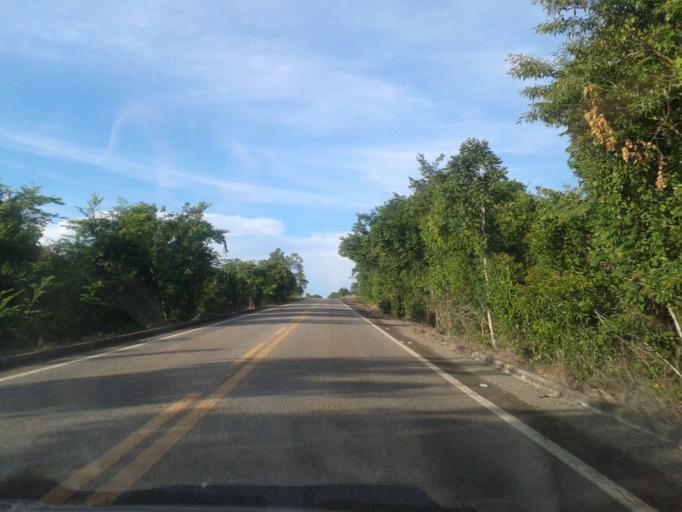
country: BR
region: Goias
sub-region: Sao Miguel Do Araguaia
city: Sao Miguel do Araguaia
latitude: -13.5449
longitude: -50.3079
